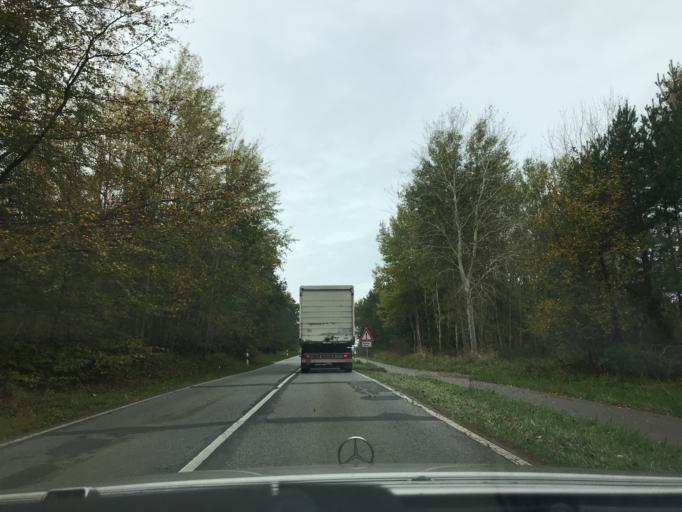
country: DE
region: Mecklenburg-Vorpommern
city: Lubmin
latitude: 54.1364
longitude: 13.6788
